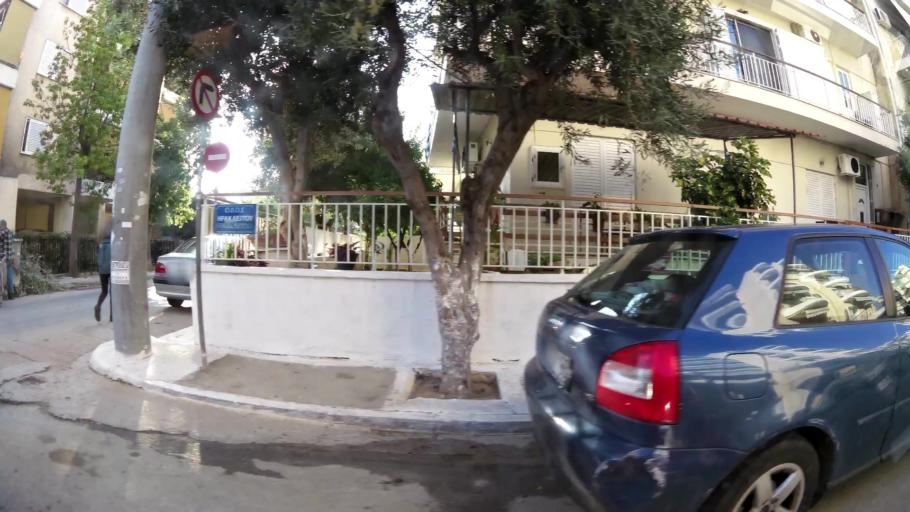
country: GR
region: Attica
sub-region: Nomarchia Anatolikis Attikis
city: Acharnes
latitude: 38.0853
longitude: 23.7410
